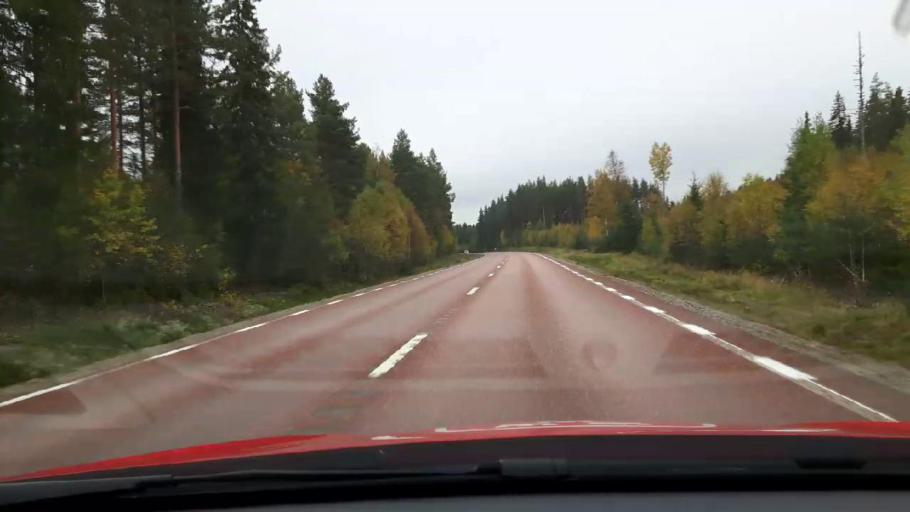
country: SE
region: Gaevleborg
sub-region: Ljusdals Kommun
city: Farila
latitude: 61.8228
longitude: 15.7564
